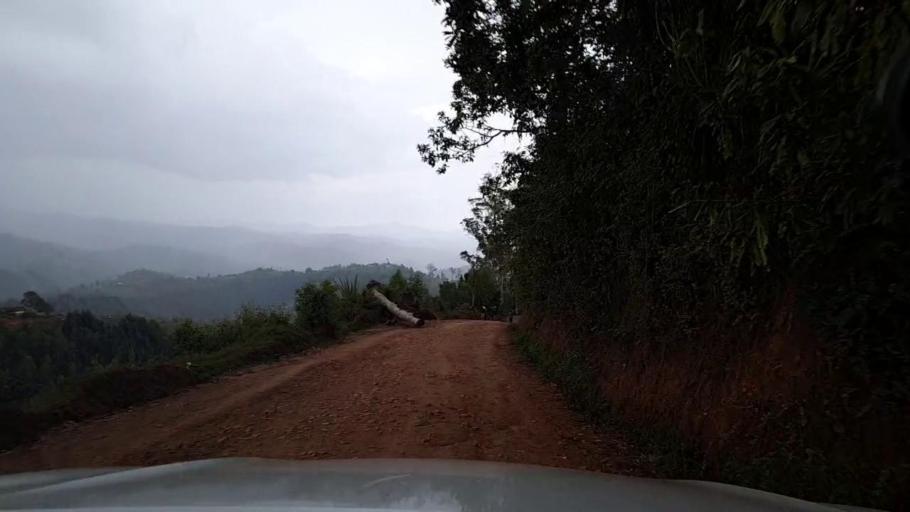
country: BI
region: Kayanza
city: Kayanza
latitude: -2.7867
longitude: 29.5311
